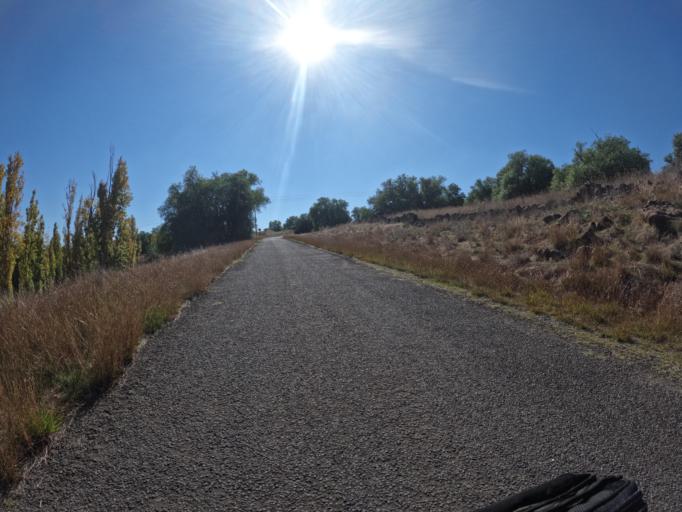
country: AU
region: Victoria
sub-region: Greater Bendigo
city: Epsom
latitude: -36.7901
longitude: 144.5109
